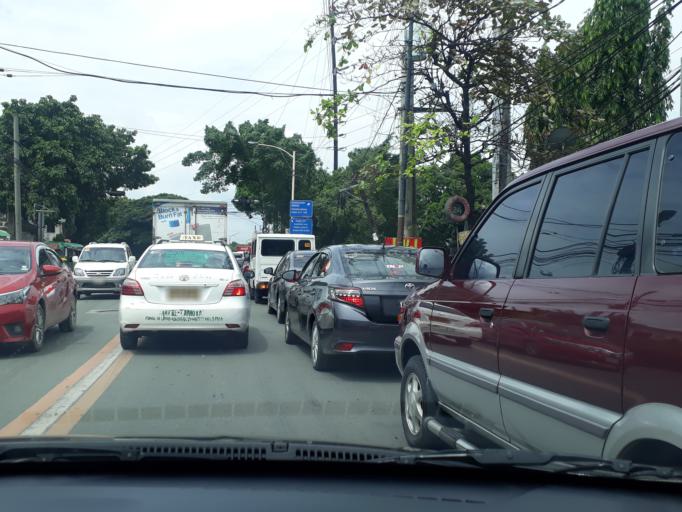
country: PH
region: Metro Manila
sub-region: Marikina
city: Calumpang
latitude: 14.5997
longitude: 121.0916
